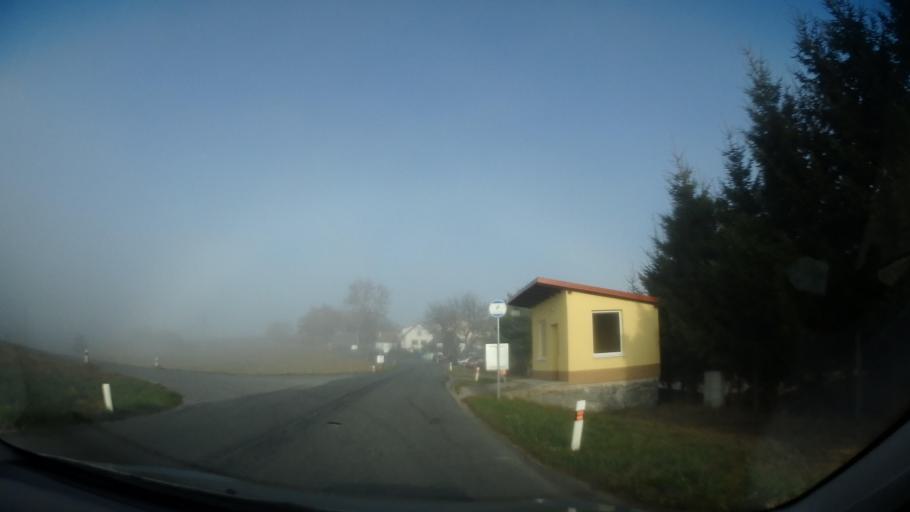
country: CZ
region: Vysocina
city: Bystrice nad Pernstejnem
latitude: 49.4149
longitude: 16.2225
